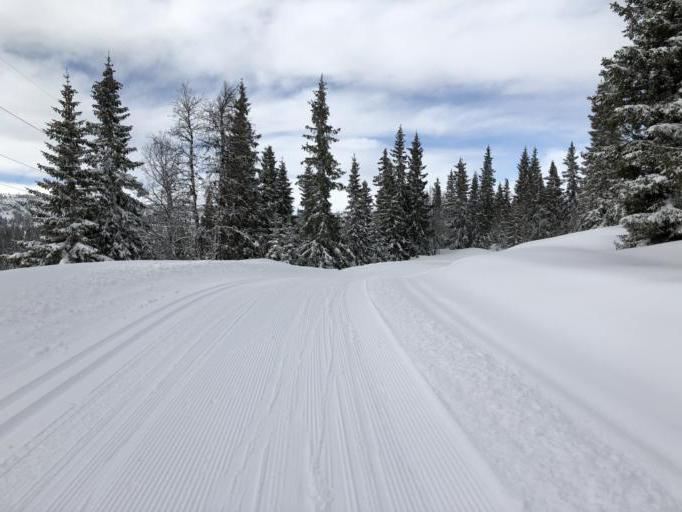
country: NO
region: Oppland
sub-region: Gausdal
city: Segalstad bru
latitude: 61.3237
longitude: 10.0786
